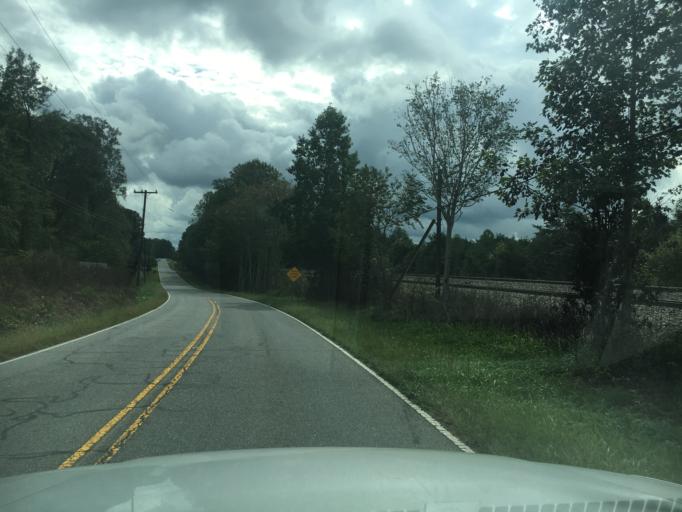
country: US
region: North Carolina
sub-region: Catawba County
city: Saint Stephens
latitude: 35.7306
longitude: -81.2847
